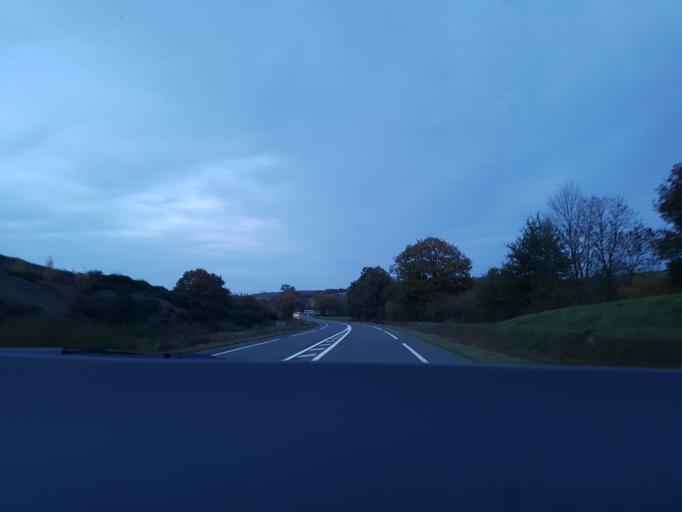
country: FR
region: Pays de la Loire
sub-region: Departement de la Mayenne
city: Montigne-le-Brillant
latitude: 48.0244
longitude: -0.8146
